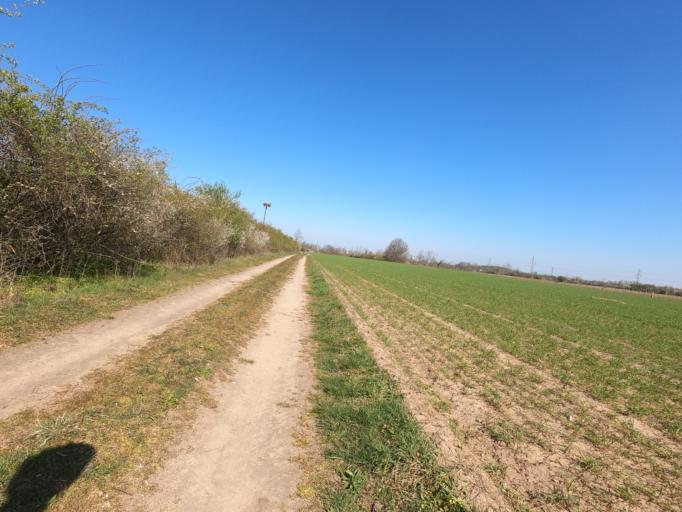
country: DE
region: Hesse
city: Morfelden-Walldorf
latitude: 49.9688
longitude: 8.5834
